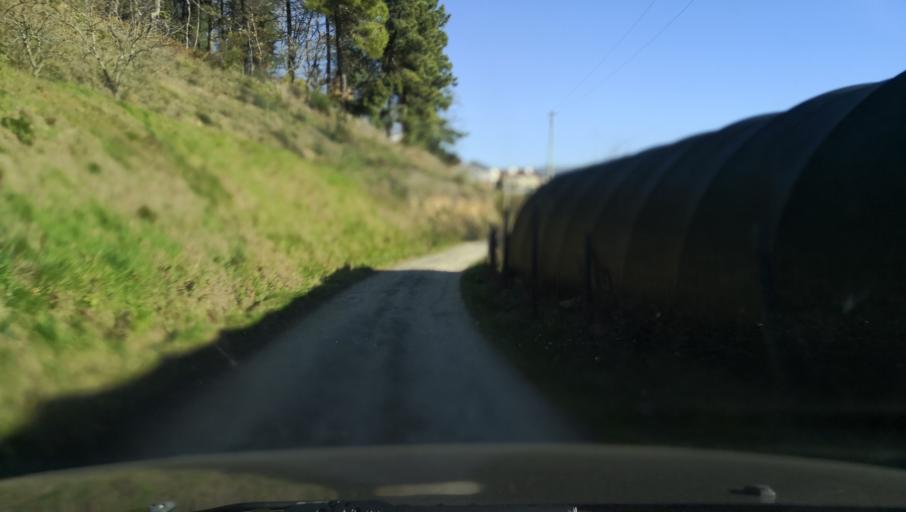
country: PT
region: Vila Real
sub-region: Vila Real
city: Vila Real
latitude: 41.3406
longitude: -7.7398
